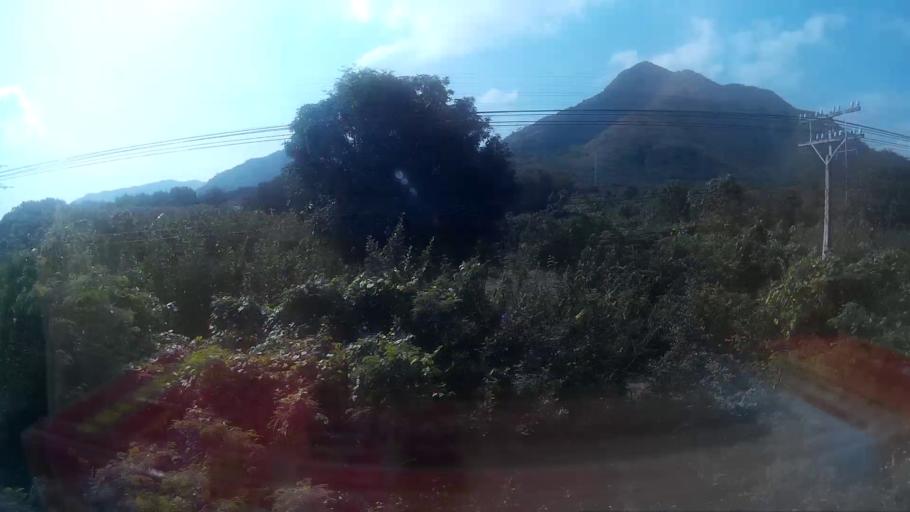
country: VN
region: Khanh Hoa
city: Ninh Hoa
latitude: 12.4003
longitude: 109.1688
